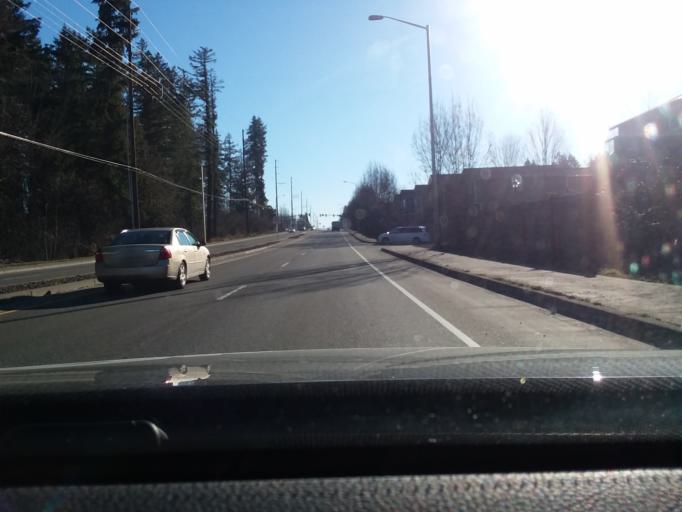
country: US
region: Washington
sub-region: Pierce County
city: Frederickson
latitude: 47.0964
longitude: -122.3340
